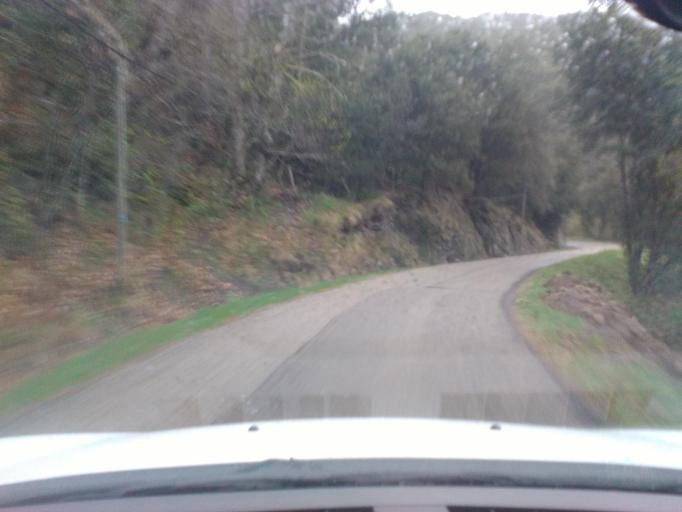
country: FR
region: Languedoc-Roussillon
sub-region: Departement du Gard
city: Valleraugue
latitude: 44.1114
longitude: 3.7055
